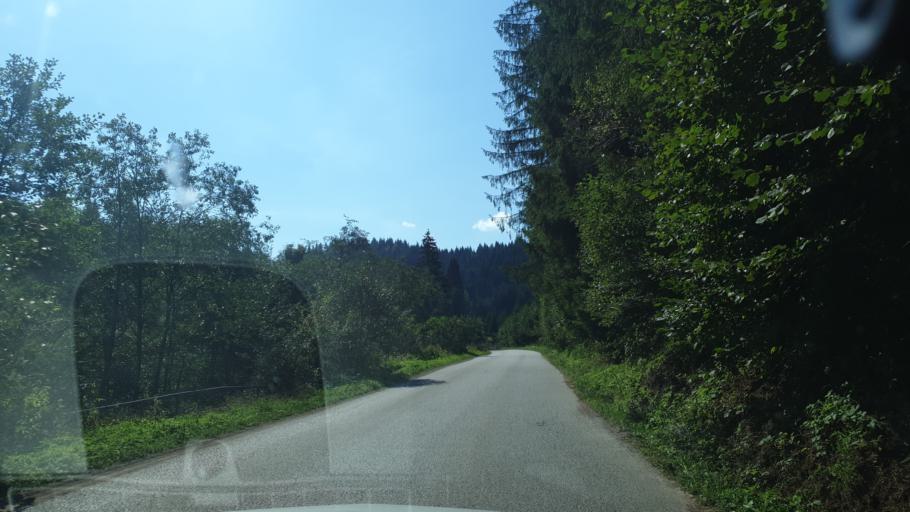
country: RS
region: Central Serbia
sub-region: Zlatiborski Okrug
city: Nova Varos
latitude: 43.4539
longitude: 19.8425
